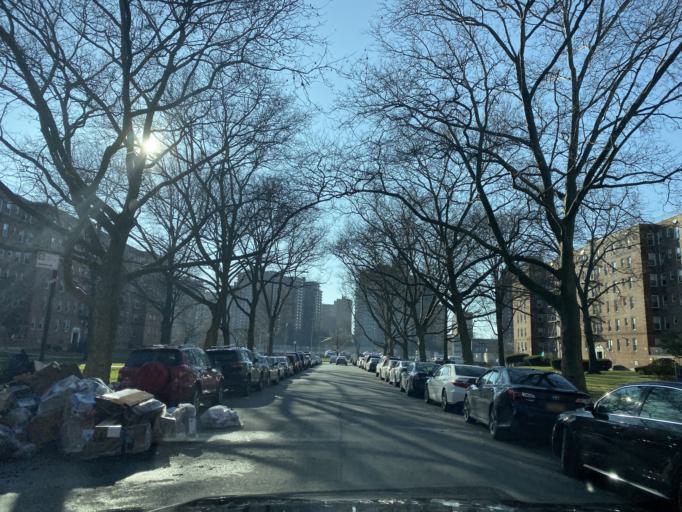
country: US
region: New York
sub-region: Kings County
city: Coney Island
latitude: 40.5851
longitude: -73.9711
